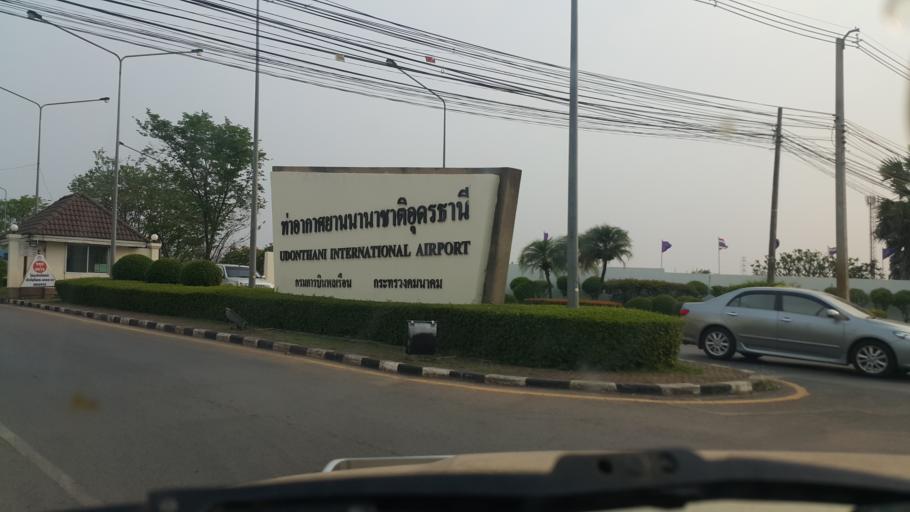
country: TH
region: Changwat Udon Thani
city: Udon Thani
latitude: 17.3897
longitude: 102.7703
